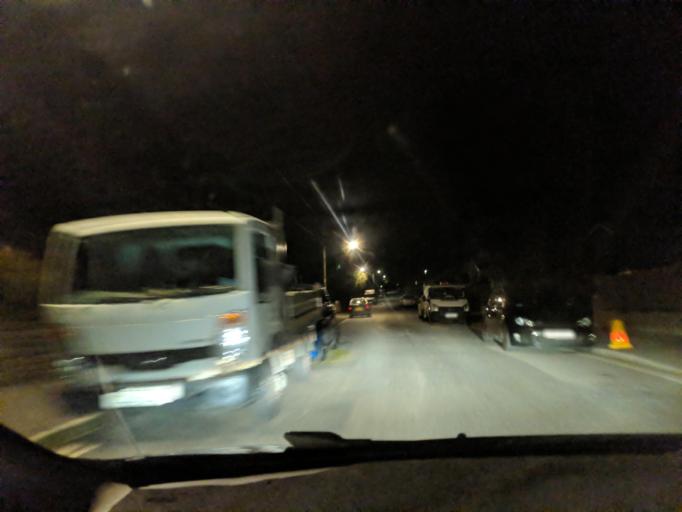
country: GB
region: England
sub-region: Cornwall
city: Mevagissey
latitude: 50.2696
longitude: -4.7940
